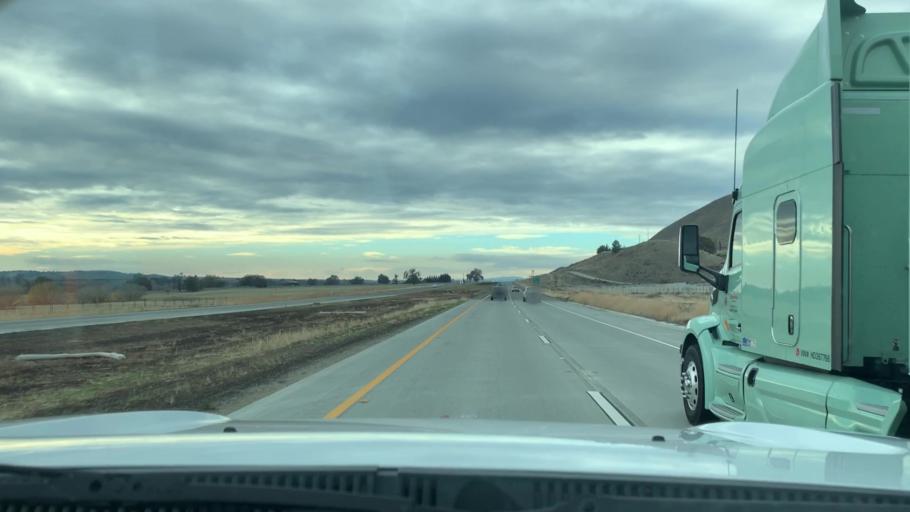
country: US
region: California
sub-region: San Luis Obispo County
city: Shandon
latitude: 35.6625
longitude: -120.4031
